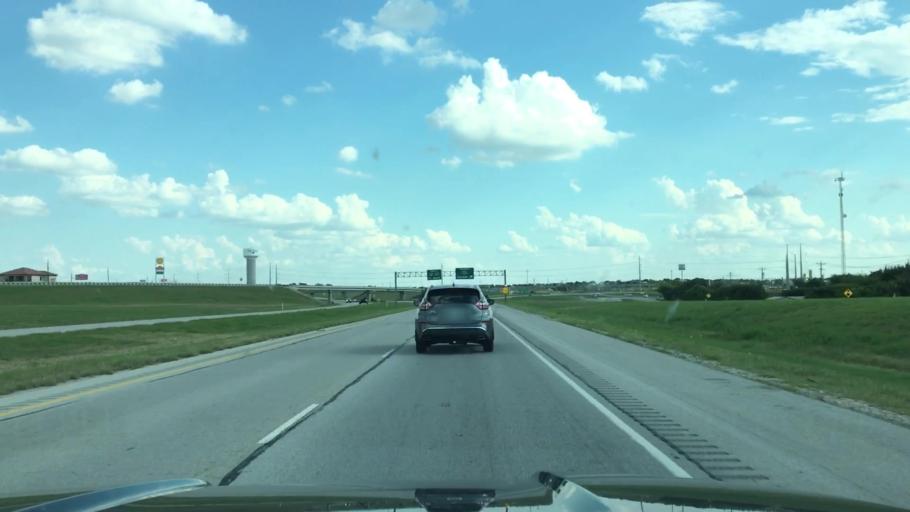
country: US
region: Texas
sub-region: Tarrant County
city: Pecan Acres
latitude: 32.9732
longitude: -97.4222
